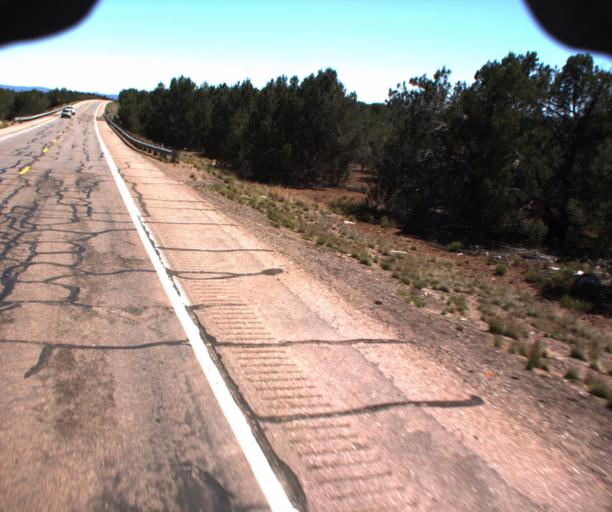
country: US
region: Arizona
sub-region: Yavapai County
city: Paulden
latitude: 35.0544
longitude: -112.3973
